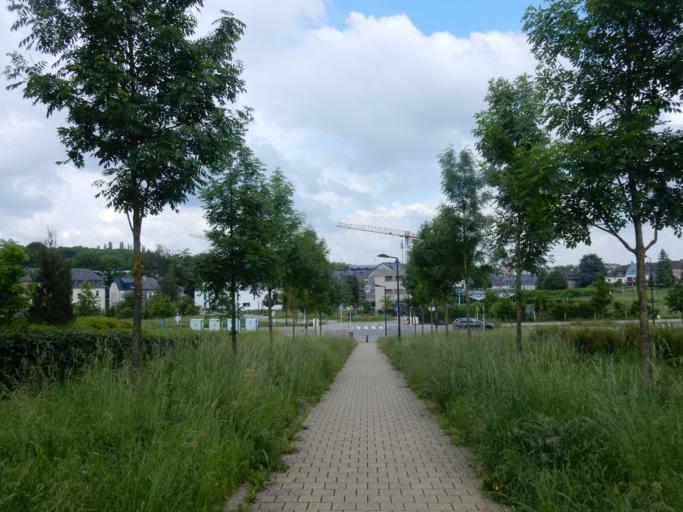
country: LU
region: Luxembourg
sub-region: Canton de Luxembourg
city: Luxembourg
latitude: 49.6104
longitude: 6.1037
